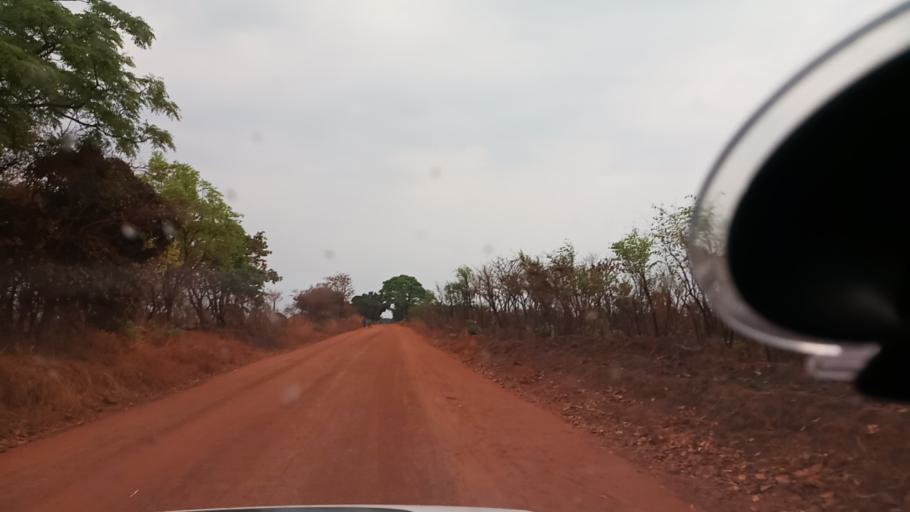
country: ZM
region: Luapula
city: Nchelenge
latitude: -9.1686
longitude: 28.2814
